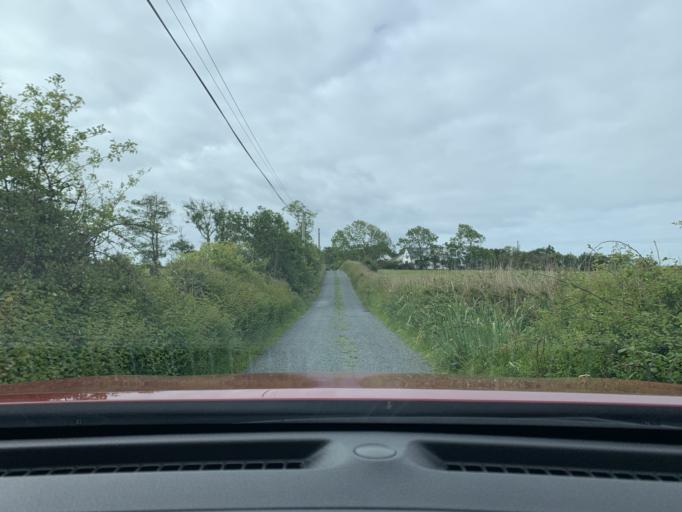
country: IE
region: Connaught
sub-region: Sligo
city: Sligo
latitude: 54.3872
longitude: -8.5222
